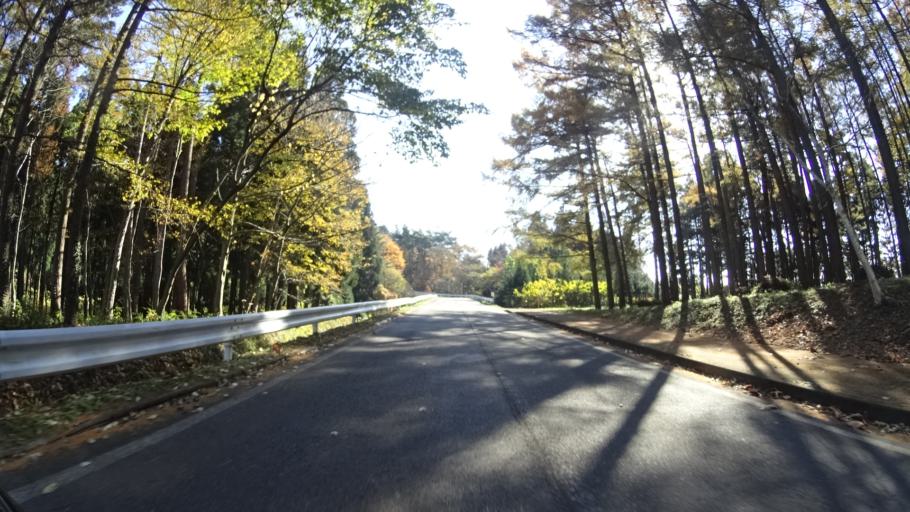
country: JP
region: Niigata
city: Itoigawa
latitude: 37.0218
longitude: 137.8674
